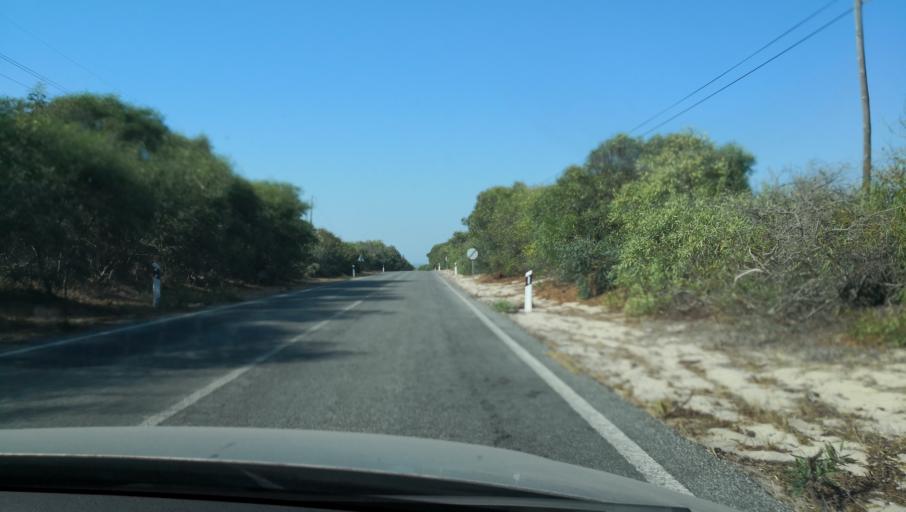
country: PT
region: Setubal
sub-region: Setubal
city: Setubal
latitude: 38.4131
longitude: -8.8147
